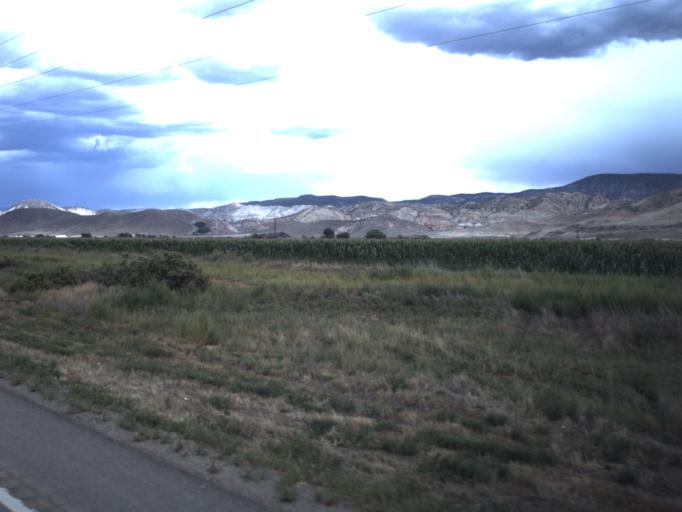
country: US
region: Utah
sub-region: Sevier County
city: Richfield
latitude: 38.8189
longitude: -112.0053
